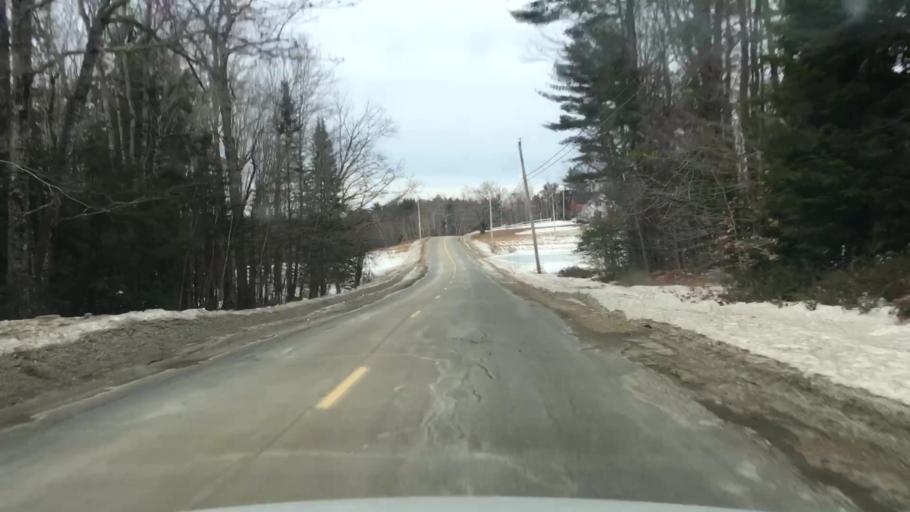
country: US
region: Maine
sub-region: Kennebec County
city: Chelsea
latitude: 44.2646
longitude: -69.6487
